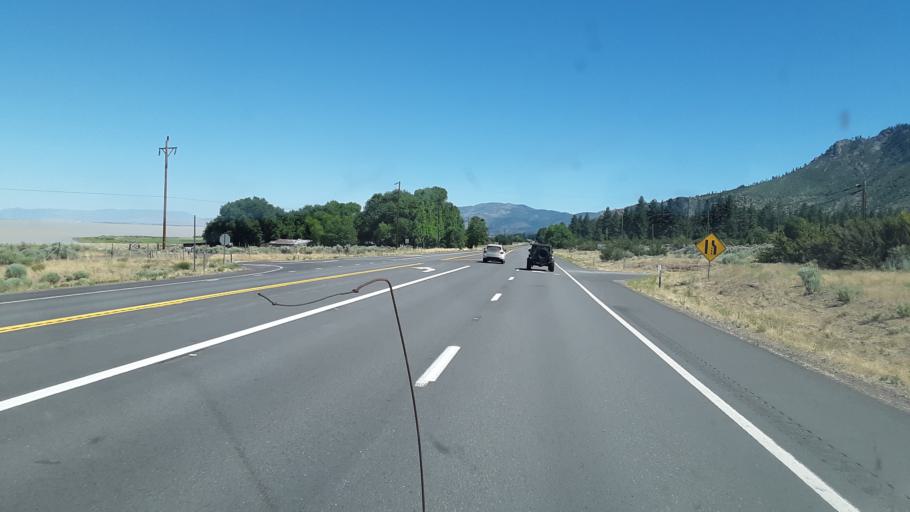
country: US
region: California
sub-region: Lassen County
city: Janesville
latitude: 40.2471
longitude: -120.4592
